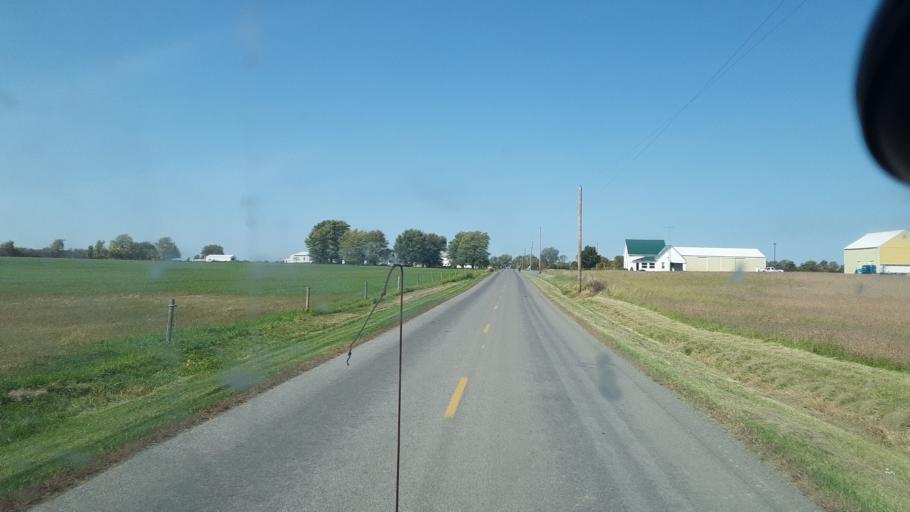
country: US
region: Ohio
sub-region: Logan County
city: Northwood
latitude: 40.4965
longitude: -83.7807
